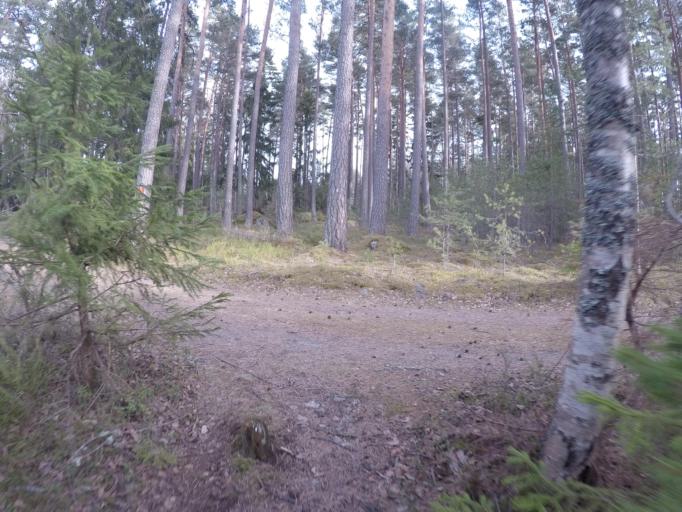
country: SE
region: Soedermanland
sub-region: Eskilstuna Kommun
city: Torshalla
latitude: 59.4485
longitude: 16.5417
